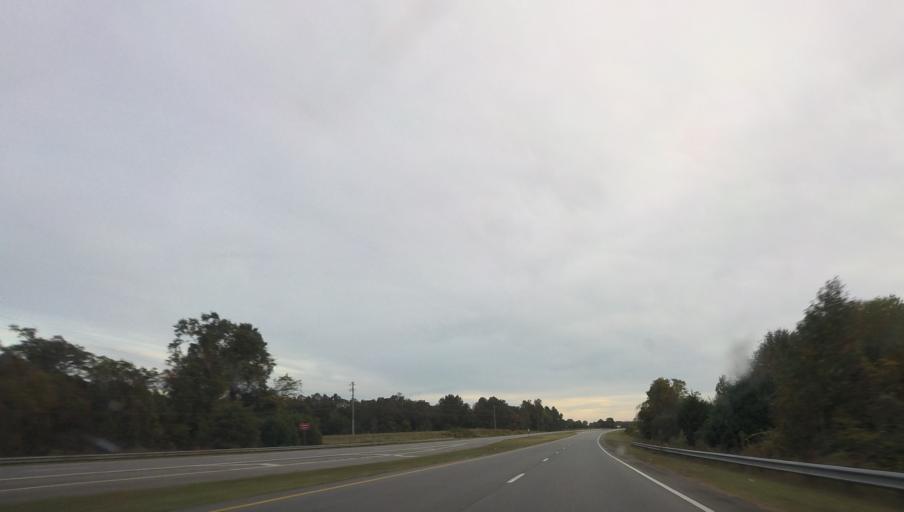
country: US
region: Georgia
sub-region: Houston County
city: Perry
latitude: 32.4627
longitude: -83.6953
